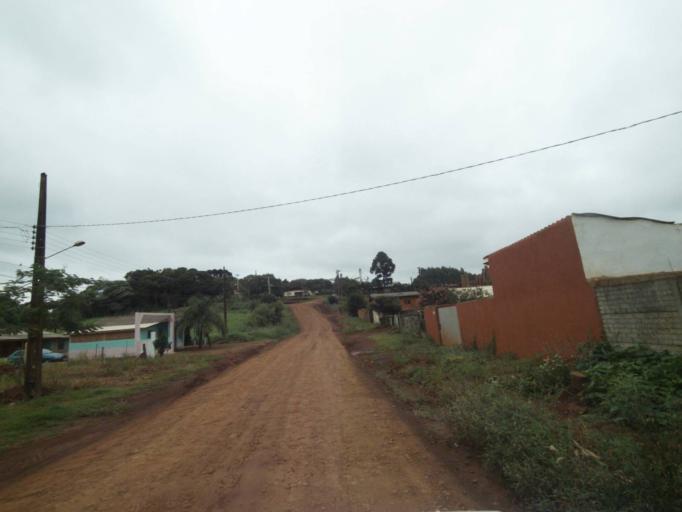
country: BR
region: Parana
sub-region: Pitanga
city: Pitanga
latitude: -24.9328
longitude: -51.8736
